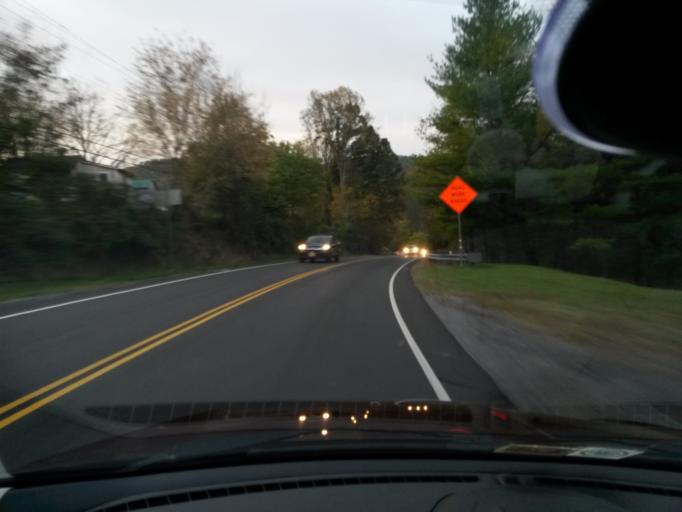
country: US
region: Virginia
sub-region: Roanoke County
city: Vinton
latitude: 37.2194
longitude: -79.8917
